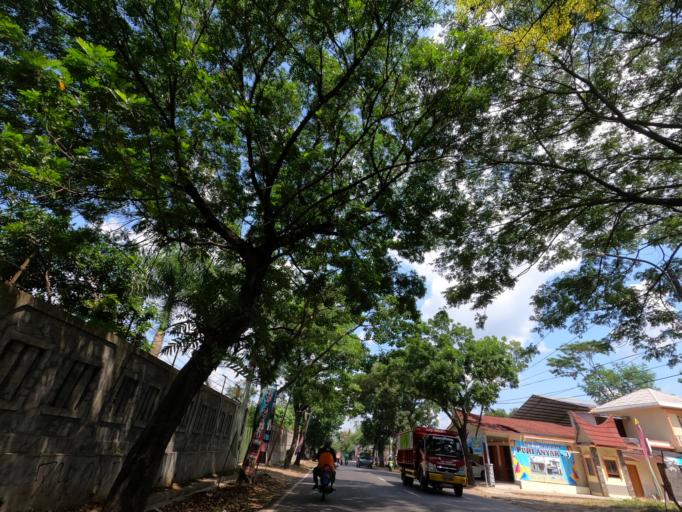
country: ID
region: West Java
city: Pamanukan
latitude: -6.5531
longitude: 107.7435
